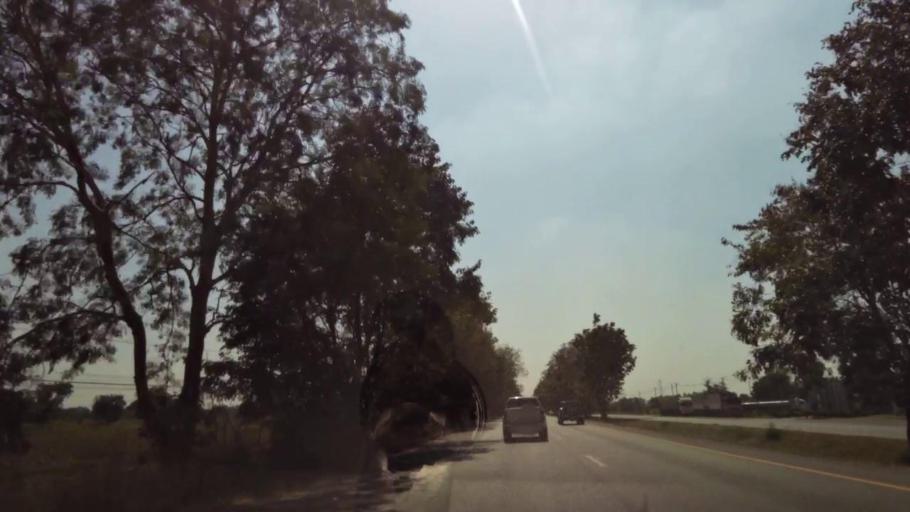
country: TH
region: Phichit
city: Wachira Barami
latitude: 16.4017
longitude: 100.1413
